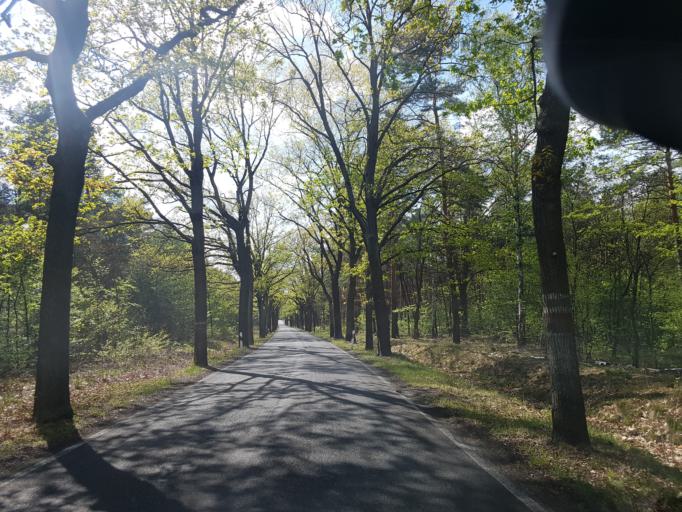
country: DE
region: Brandenburg
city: Cottbus
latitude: 51.6795
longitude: 14.3970
